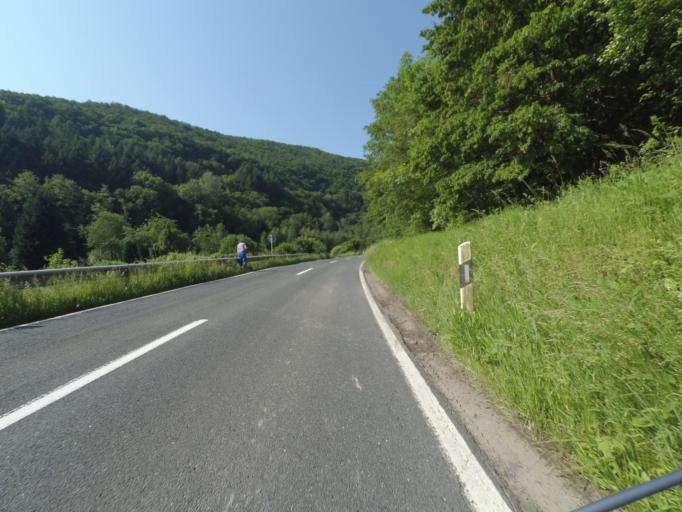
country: DE
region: Rheinland-Pfalz
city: Pommern
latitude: 50.1649
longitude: 7.2961
